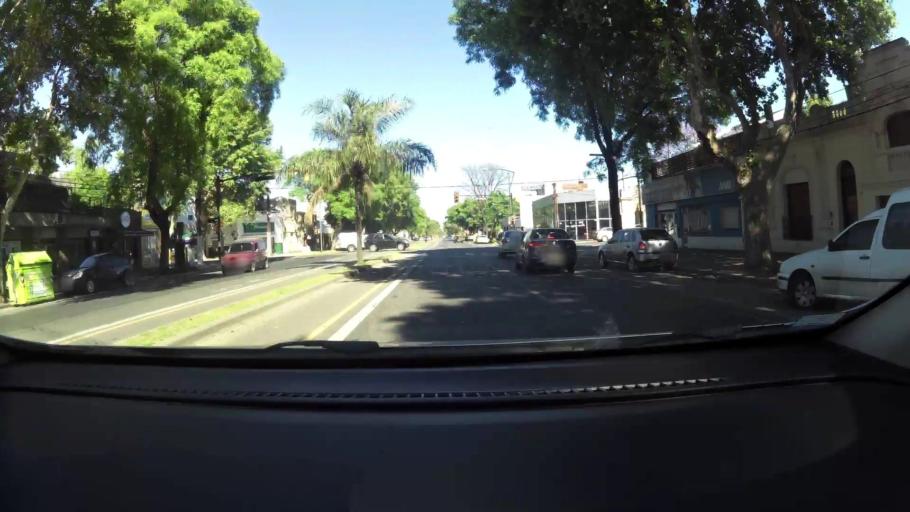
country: AR
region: Santa Fe
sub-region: Departamento de Rosario
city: Rosario
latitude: -32.9512
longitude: -60.6747
